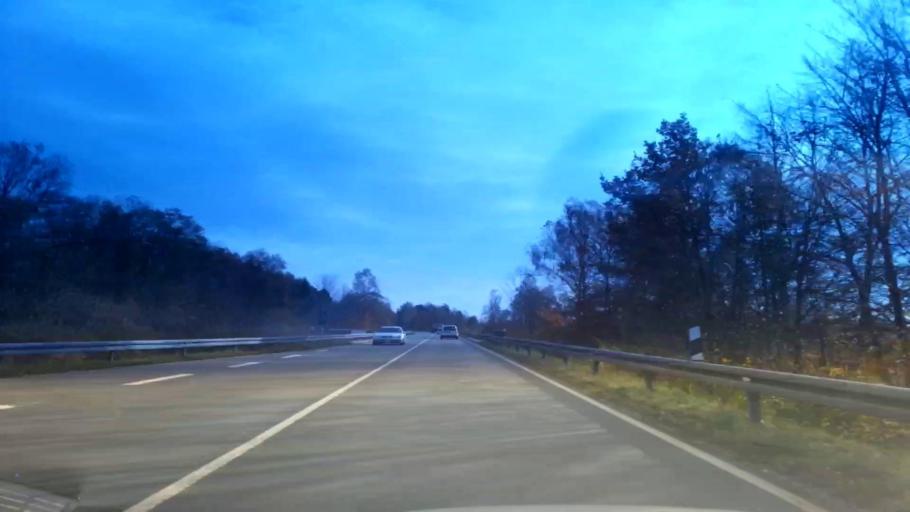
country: DE
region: Bavaria
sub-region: Upper Franconia
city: Seybothenreuth
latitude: 49.9461
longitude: 11.7223
